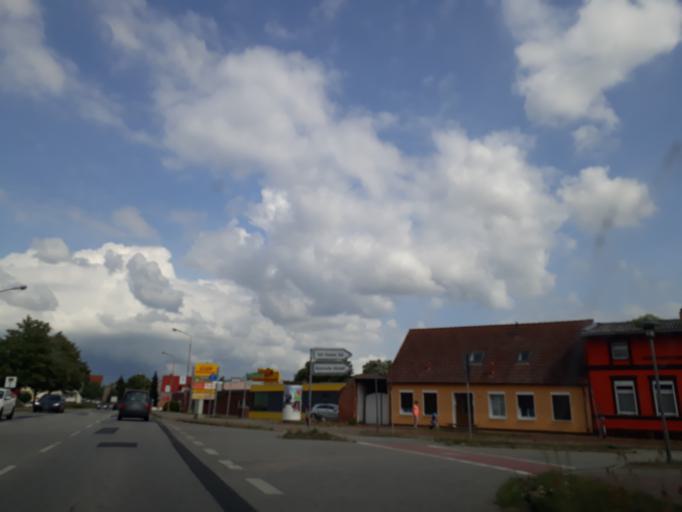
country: DE
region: Mecklenburg-Vorpommern
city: Usedom
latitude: 53.8768
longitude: 13.9230
